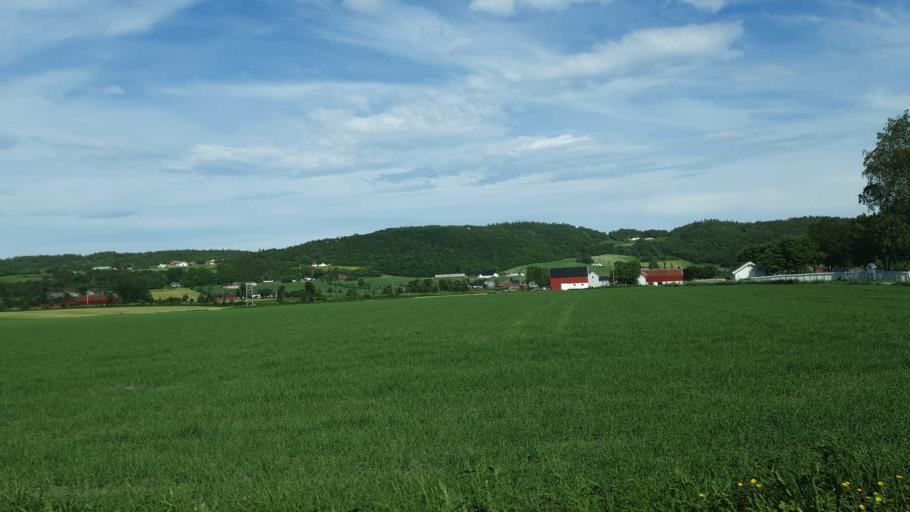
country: NO
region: Sor-Trondelag
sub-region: Rissa
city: Rissa
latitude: 63.4994
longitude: 10.0085
